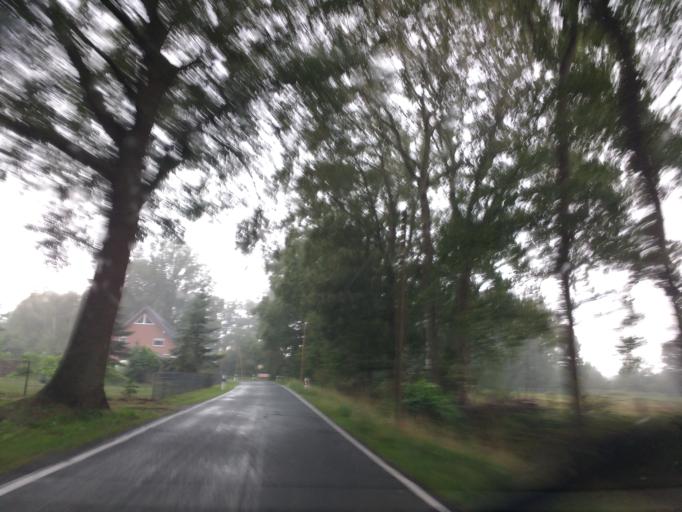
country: DE
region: North Rhine-Westphalia
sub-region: Regierungsbezirk Munster
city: Ostbevern
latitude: 52.1121
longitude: 7.8893
